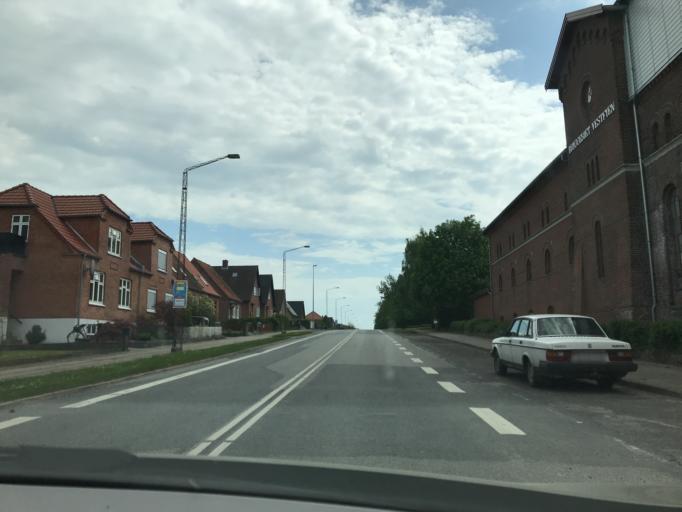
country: DK
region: South Denmark
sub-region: Assens Kommune
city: Assens
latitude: 55.2651
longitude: 9.9038
